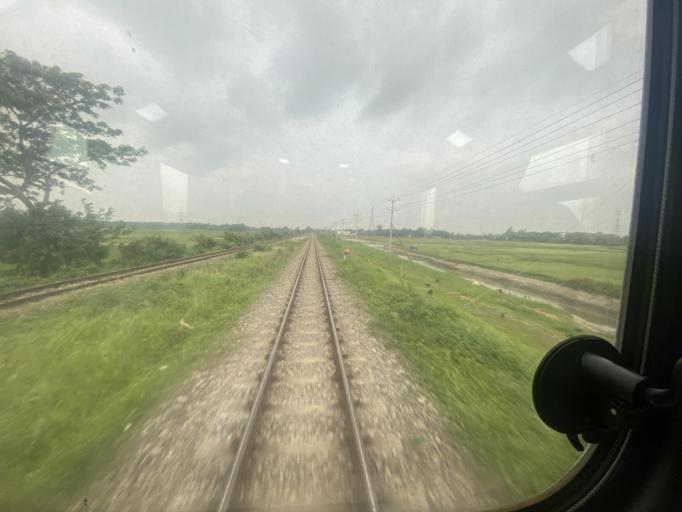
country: BD
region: Dhaka
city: Tungi
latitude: 23.9331
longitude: 90.5057
